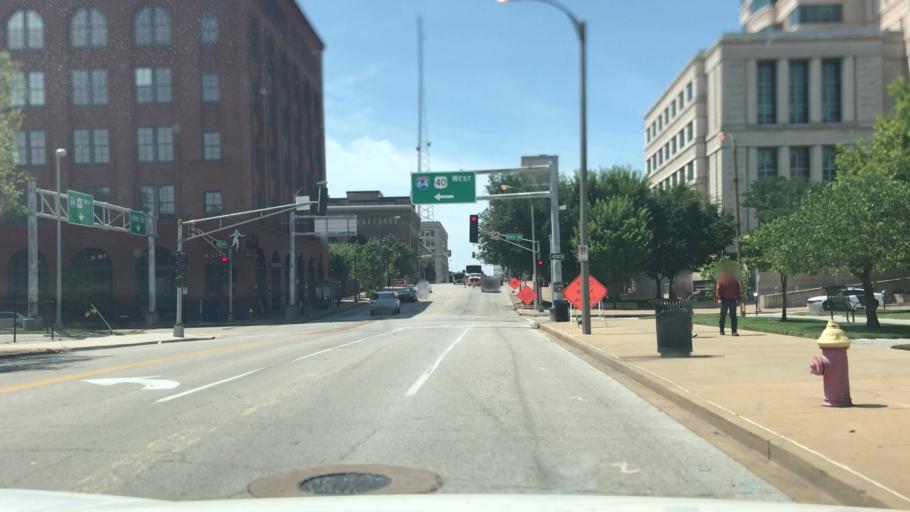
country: US
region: Missouri
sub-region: City of Saint Louis
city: St. Louis
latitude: 38.6245
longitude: -90.1958
